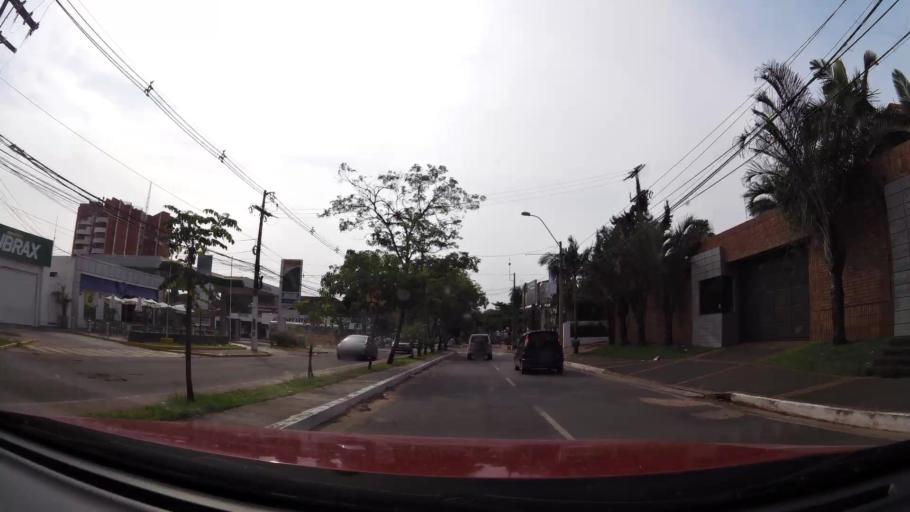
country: PY
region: Asuncion
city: Asuncion
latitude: -25.2760
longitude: -57.5666
